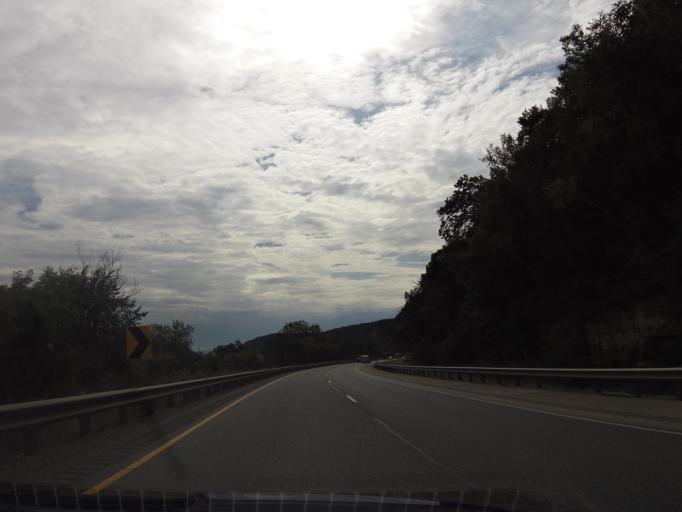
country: US
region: Wisconsin
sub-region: Trempealeau County
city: Trempealeau
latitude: 43.9317
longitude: -91.4165
